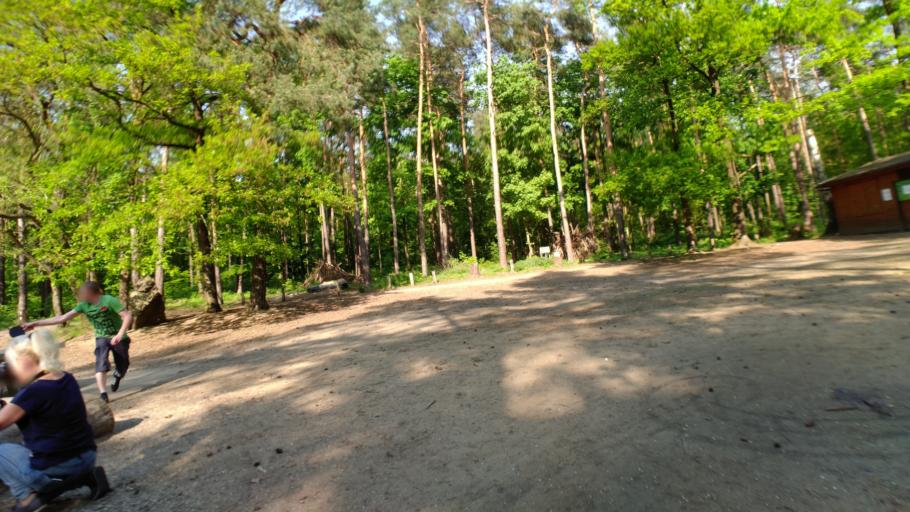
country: DE
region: Saxony
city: Albertstadt
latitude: 51.0697
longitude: 13.7919
